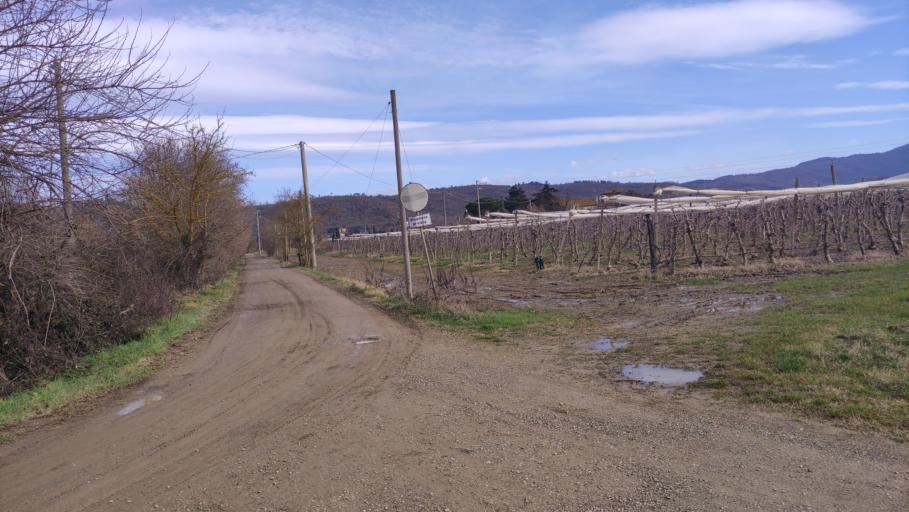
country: IT
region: Tuscany
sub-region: Province of Arezzo
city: Battifolle-Ruscello-Poggiola
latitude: 43.4368
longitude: 11.8064
